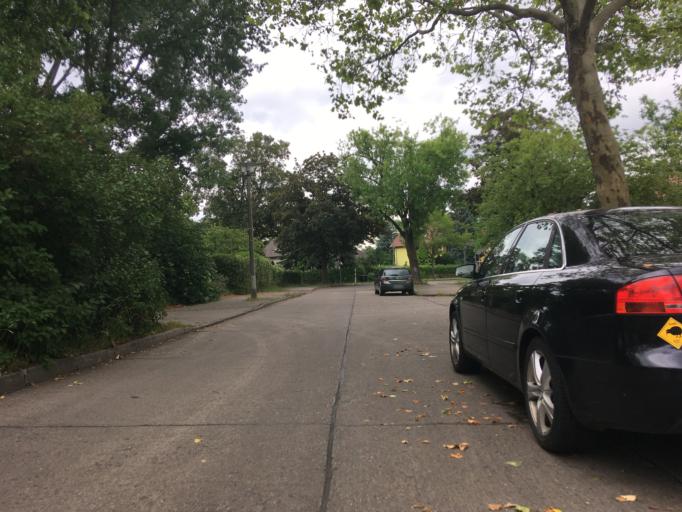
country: DE
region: Berlin
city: Friedrichshagen
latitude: 52.4512
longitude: 13.6393
